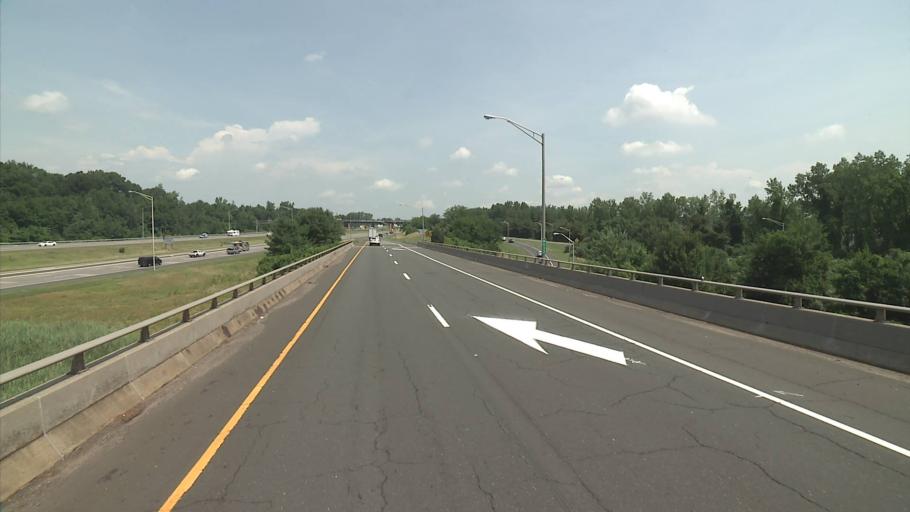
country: US
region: Connecticut
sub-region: Hartford County
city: Manchester
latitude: 41.7903
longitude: -72.5619
